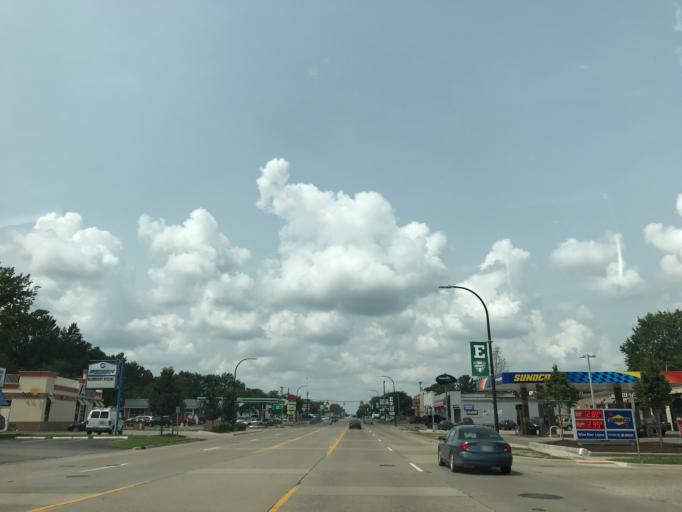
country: US
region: Michigan
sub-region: Washtenaw County
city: Ypsilanti
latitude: 42.2470
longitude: -83.6345
